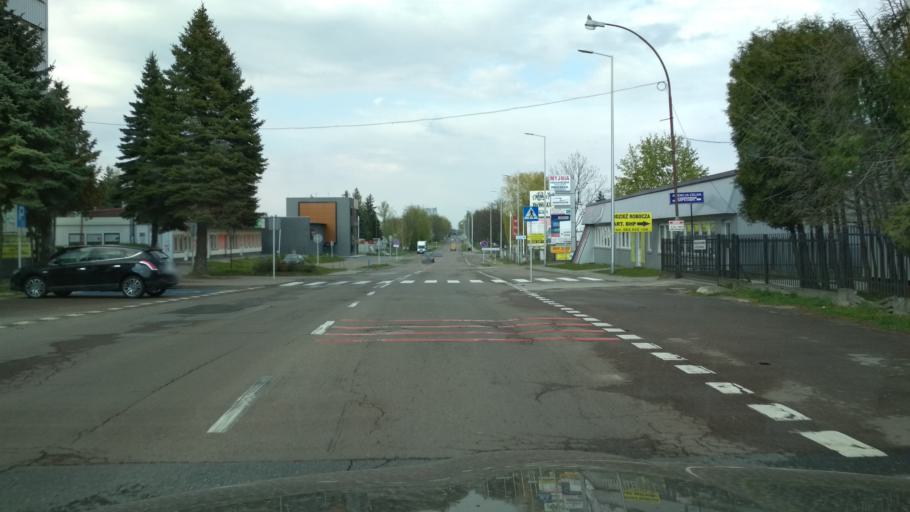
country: PL
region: Subcarpathian Voivodeship
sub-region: Powiat rzeszowski
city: Kielanowka
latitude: 50.0182
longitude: 21.9645
